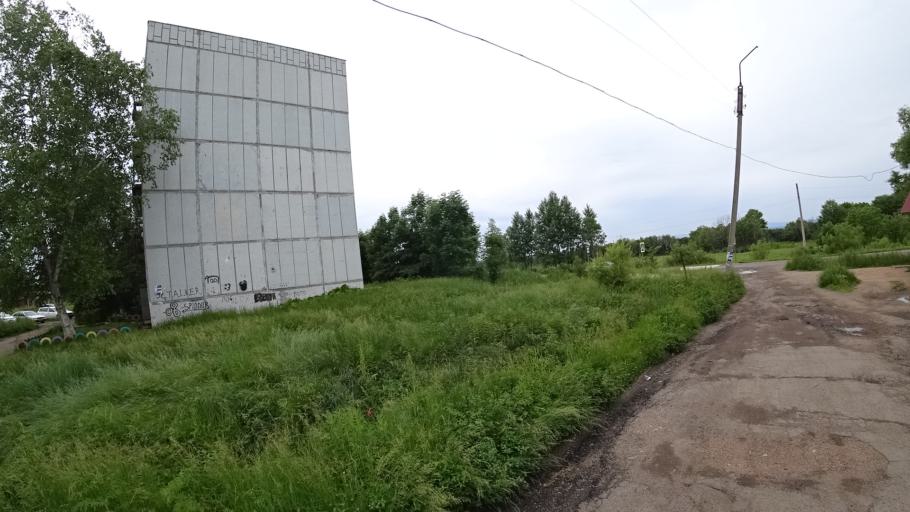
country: RU
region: Primorskiy
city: Novosysoyevka
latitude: 44.1826
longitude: 133.3512
